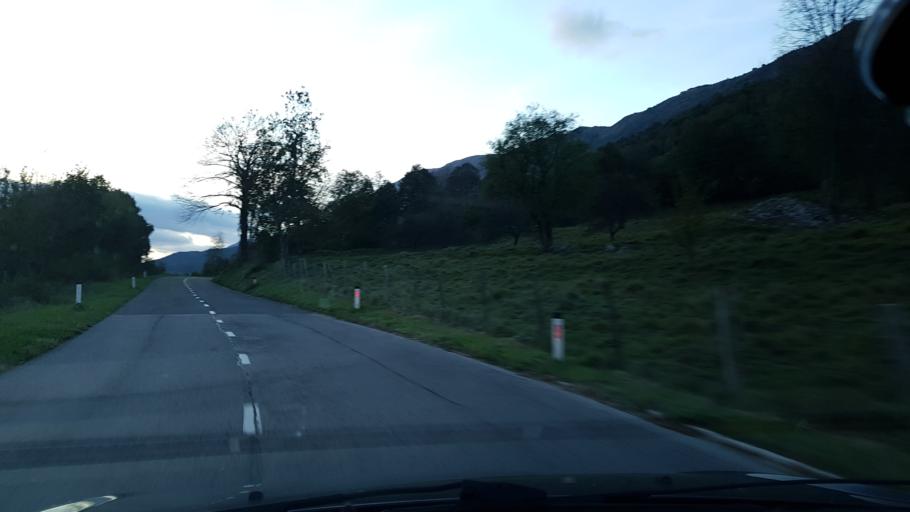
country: SI
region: Kobarid
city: Kobarid
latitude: 46.2472
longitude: 13.5245
